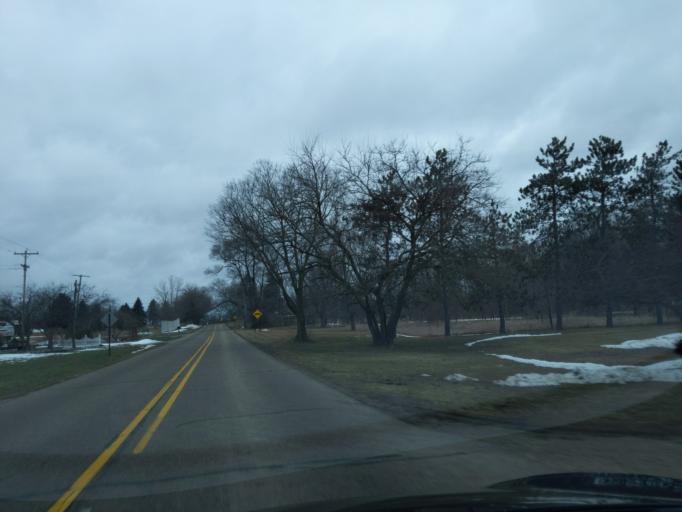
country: US
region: Michigan
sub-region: Eaton County
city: Eaton Rapids
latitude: 42.5366
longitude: -84.6280
